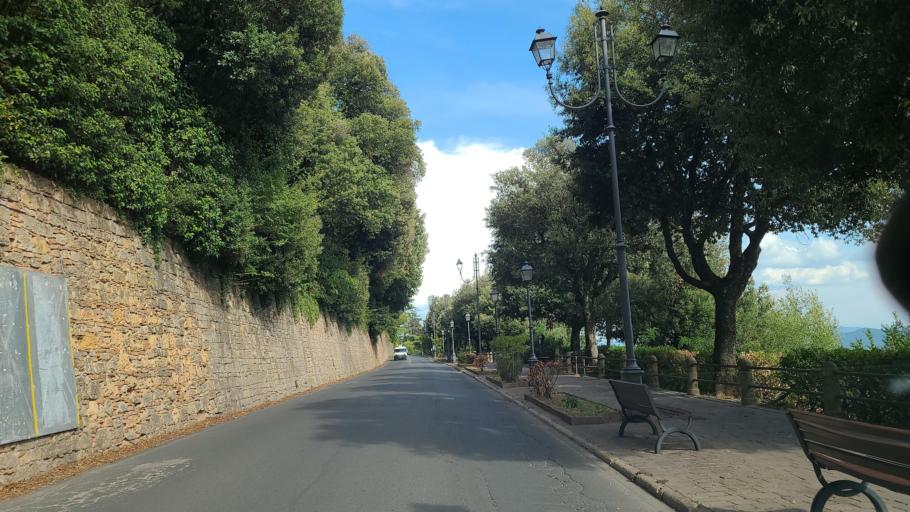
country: IT
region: Tuscany
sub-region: Province of Pisa
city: Volterra
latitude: 43.3999
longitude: 10.8614
